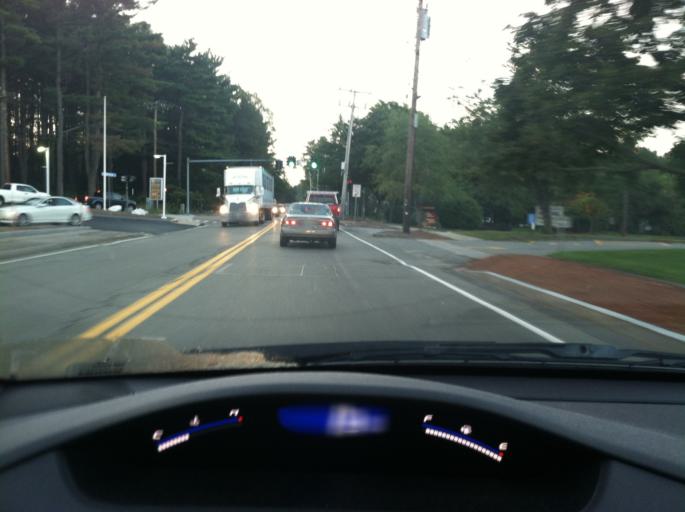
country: US
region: Massachusetts
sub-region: Middlesex County
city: Bedford
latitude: 42.4846
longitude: -71.2601
